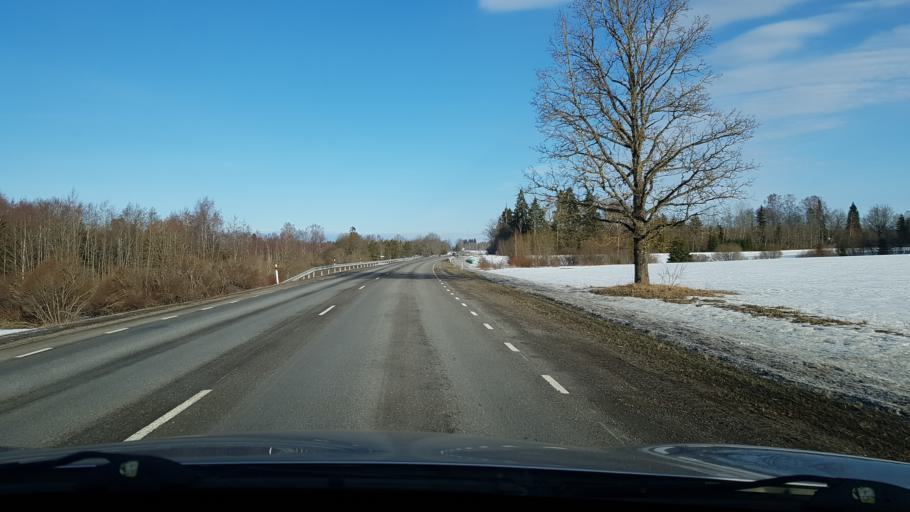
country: EE
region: Viljandimaa
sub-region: Viljandi linn
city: Viljandi
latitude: 58.4342
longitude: 25.5947
